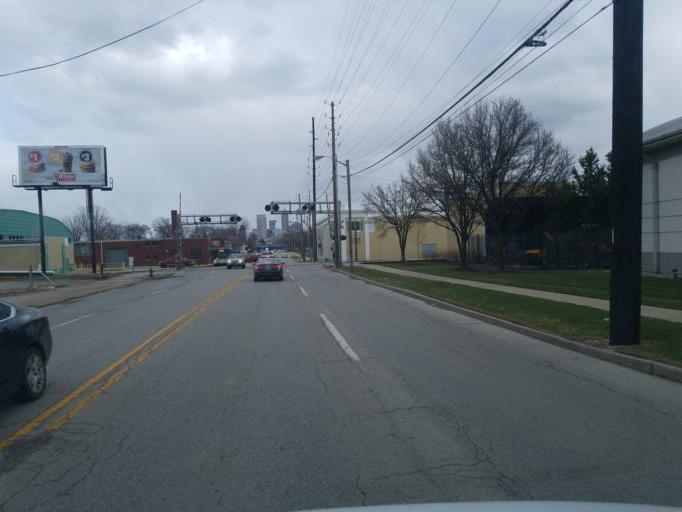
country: US
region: Indiana
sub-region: Marion County
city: Indianapolis
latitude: 39.7668
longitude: -86.1915
